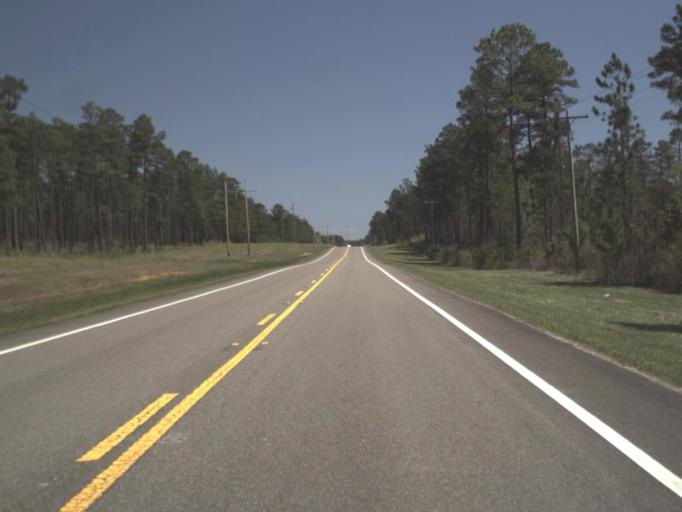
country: US
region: Florida
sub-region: Santa Rosa County
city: Point Baker
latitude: 30.8693
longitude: -86.9252
